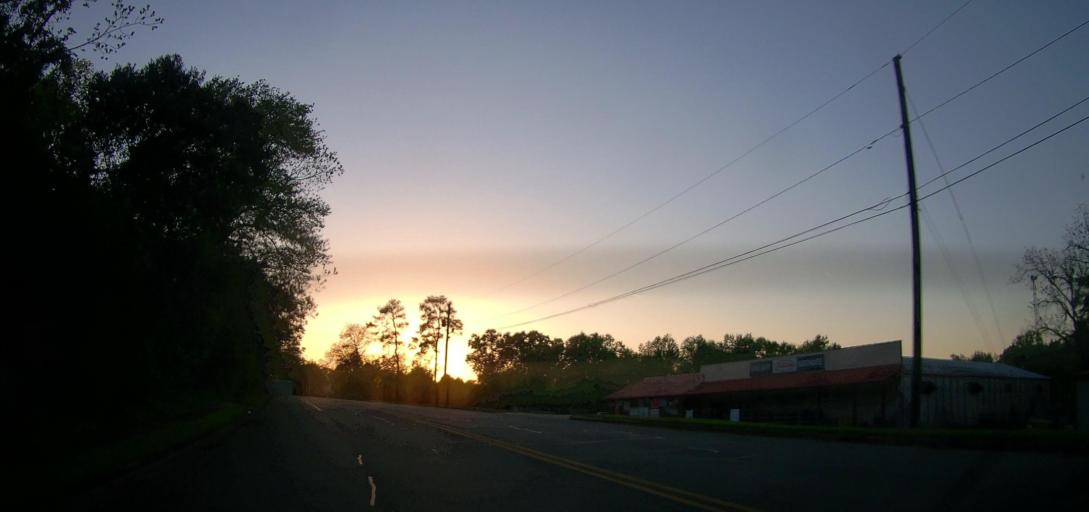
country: US
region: Georgia
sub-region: Marion County
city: Buena Vista
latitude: 32.3243
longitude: -84.5200
